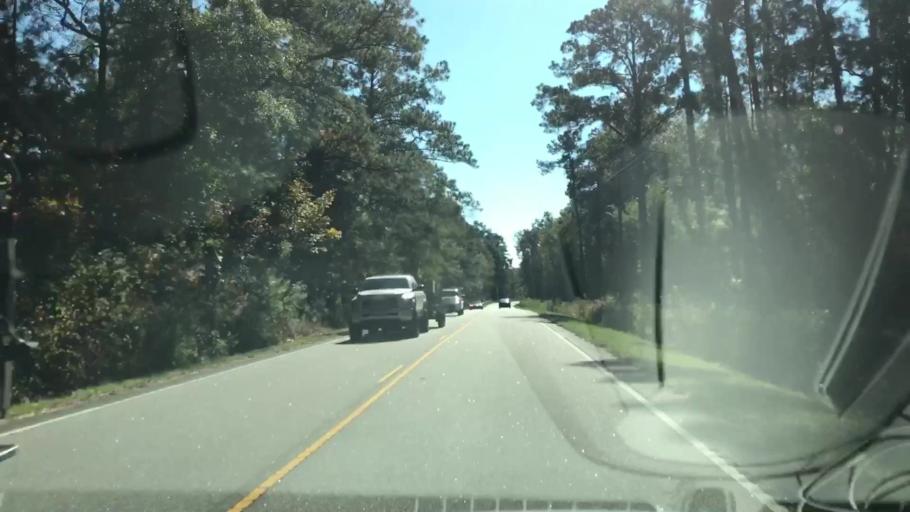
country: US
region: South Carolina
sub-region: Jasper County
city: Ridgeland
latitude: 32.4831
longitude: -80.8849
